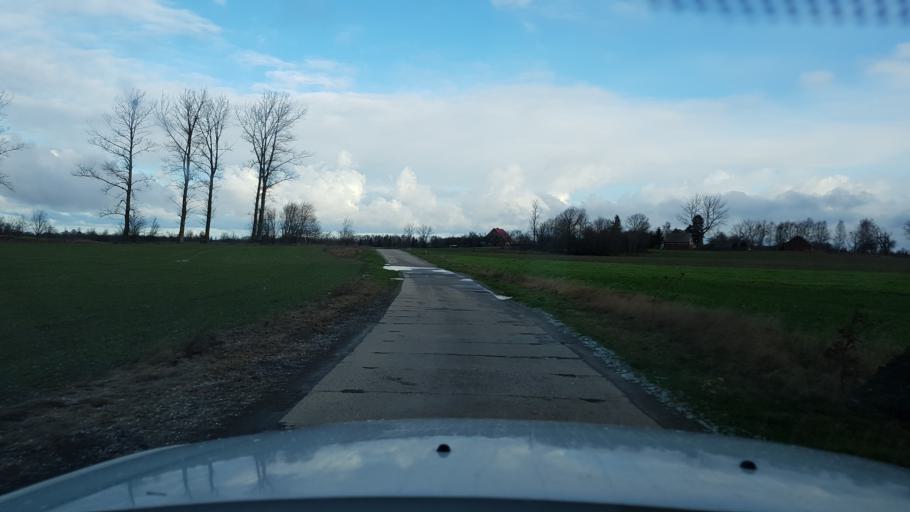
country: PL
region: West Pomeranian Voivodeship
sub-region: Powiat gryficki
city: Brojce
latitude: 54.0464
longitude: 15.3935
